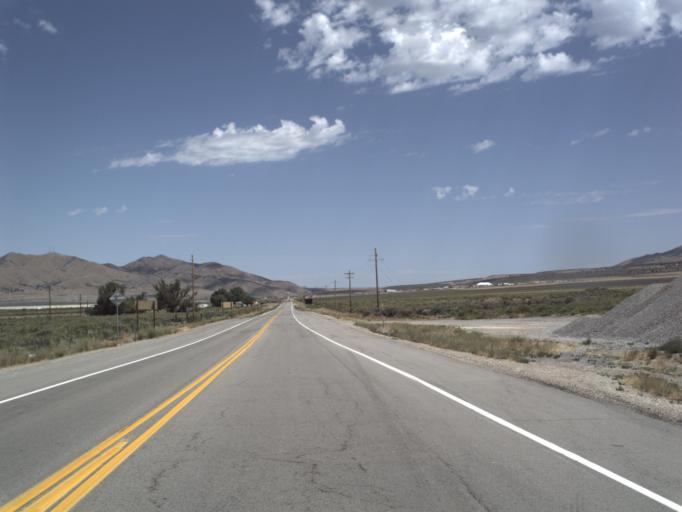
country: US
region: Utah
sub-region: Tooele County
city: Tooele
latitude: 40.3801
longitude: -112.3873
